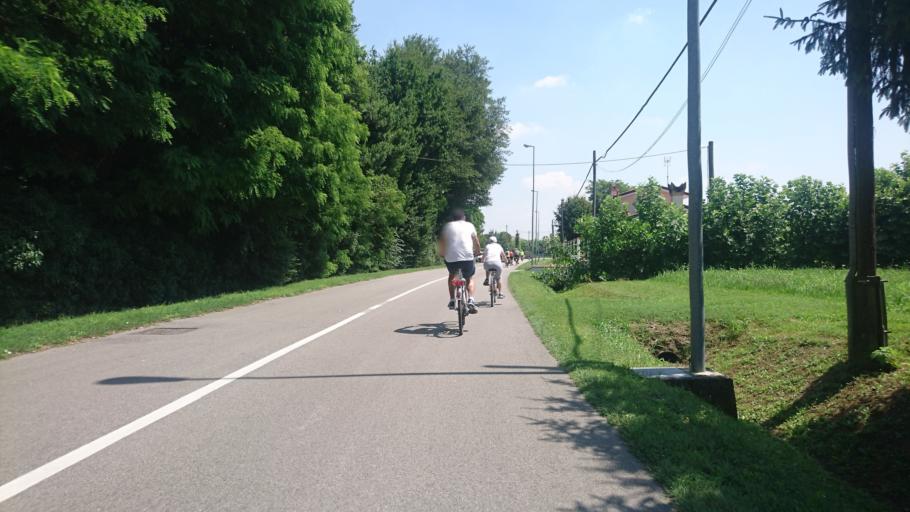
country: IT
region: Veneto
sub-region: Provincia di Venezia
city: Galta
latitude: 45.4036
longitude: 12.0254
